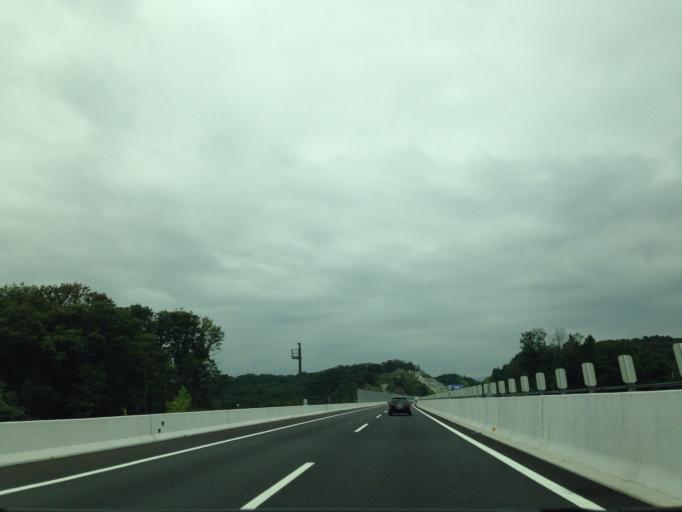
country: JP
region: Aichi
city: Okazaki
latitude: 35.0054
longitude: 137.2295
